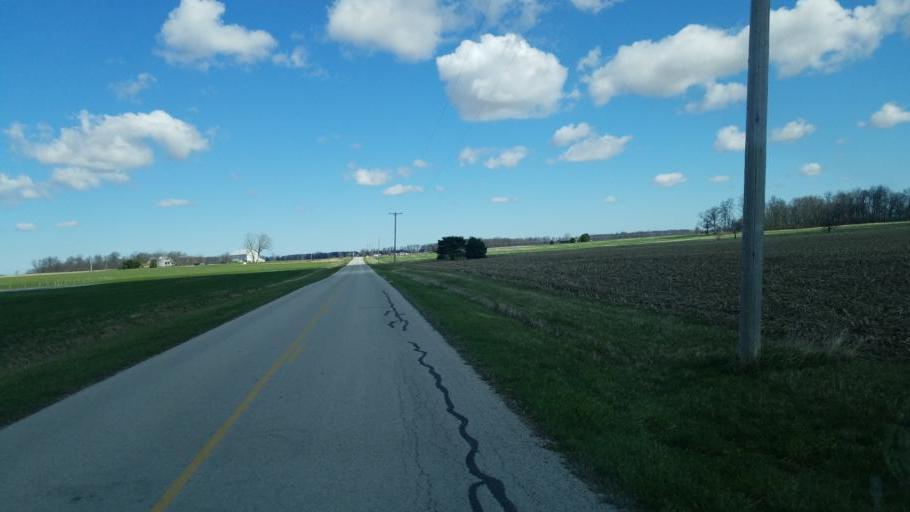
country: US
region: Ohio
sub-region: Sandusky County
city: Mount Carmel
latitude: 41.2010
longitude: -82.9374
